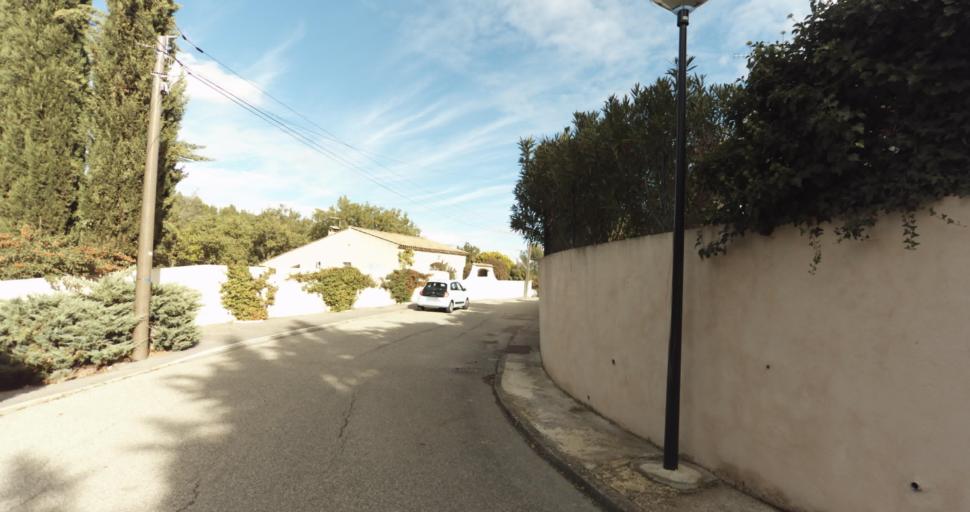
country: FR
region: Provence-Alpes-Cote d'Azur
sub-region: Departement des Bouches-du-Rhone
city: Venelles
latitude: 43.6041
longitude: 5.4827
